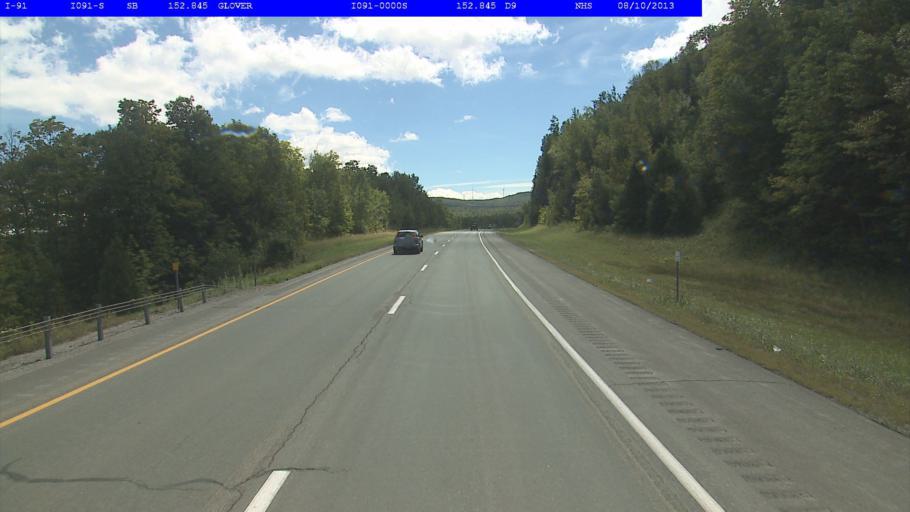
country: US
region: Vermont
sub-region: Caledonia County
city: Lyndonville
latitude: 44.7029
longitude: -72.1490
